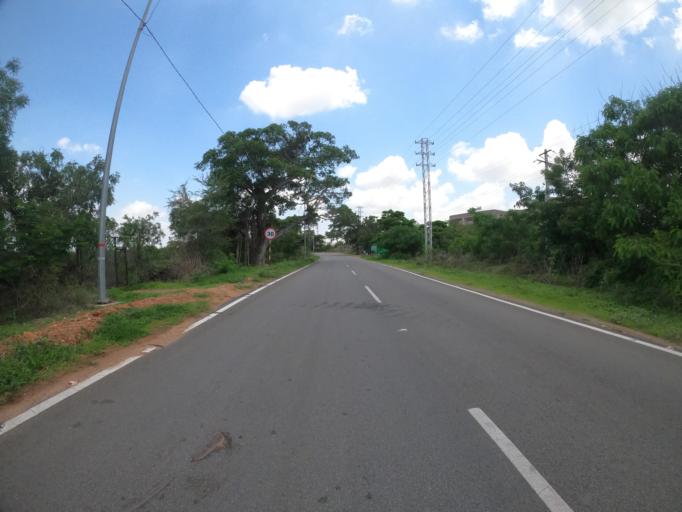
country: IN
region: Telangana
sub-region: Rangareddi
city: Sriramnagar
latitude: 17.3593
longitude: 78.3228
